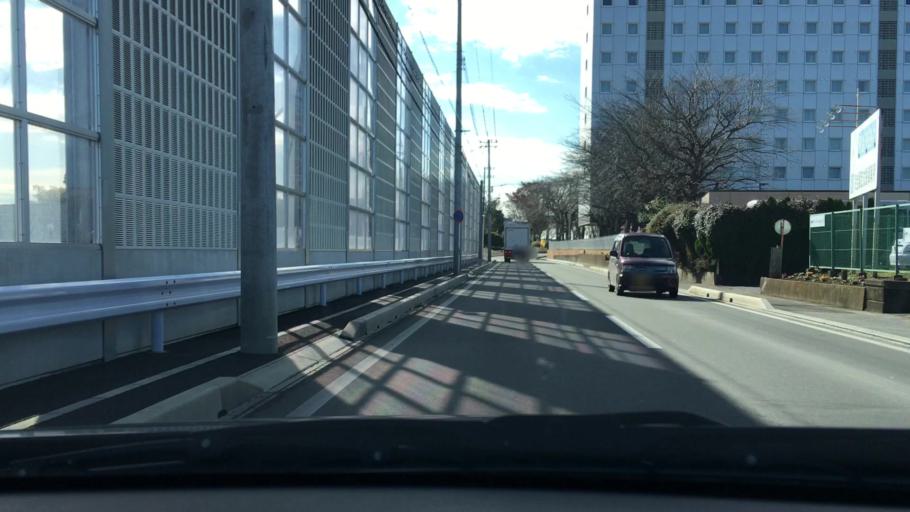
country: JP
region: Chiba
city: Narita
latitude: 35.7831
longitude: 140.3851
